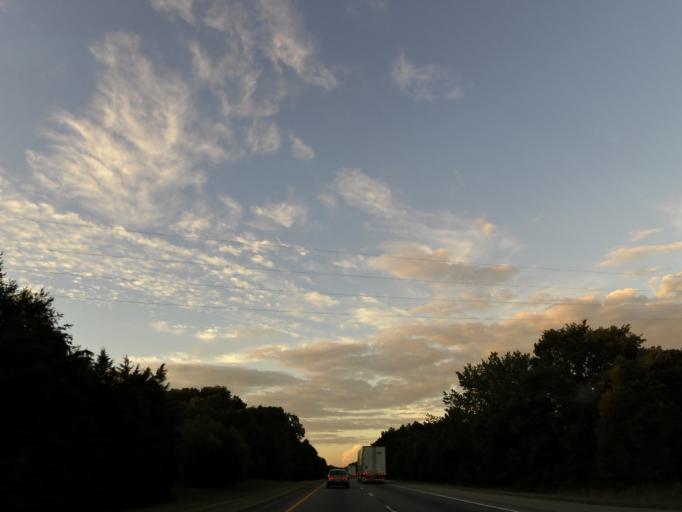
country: US
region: Tennessee
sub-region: Monroe County
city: Sweetwater
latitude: 35.5557
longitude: -84.5575
